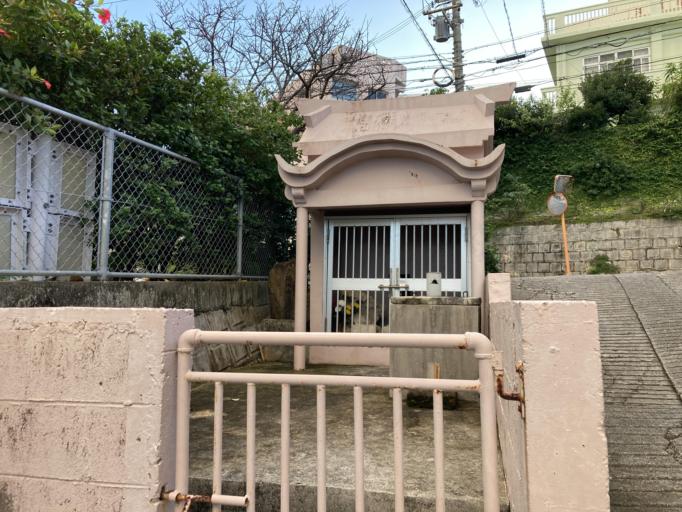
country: JP
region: Okinawa
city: Naha-shi
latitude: 26.2229
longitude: 127.7241
